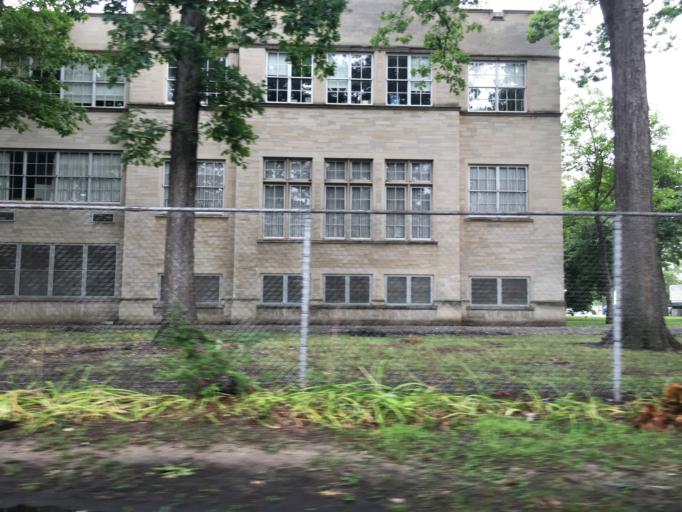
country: US
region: Michigan
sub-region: Oakland County
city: Ferndale
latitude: 42.4139
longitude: -83.1542
